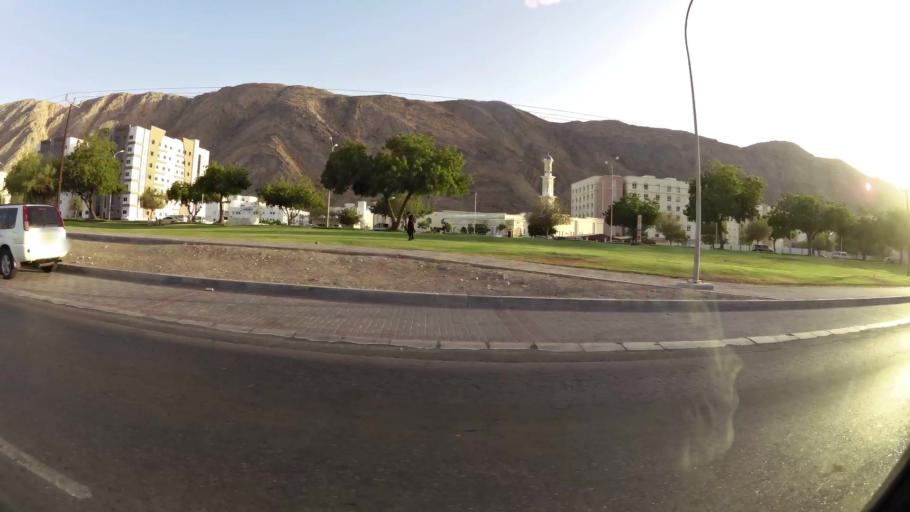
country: OM
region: Muhafazat Masqat
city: Muscat
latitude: 23.5685
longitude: 58.5748
